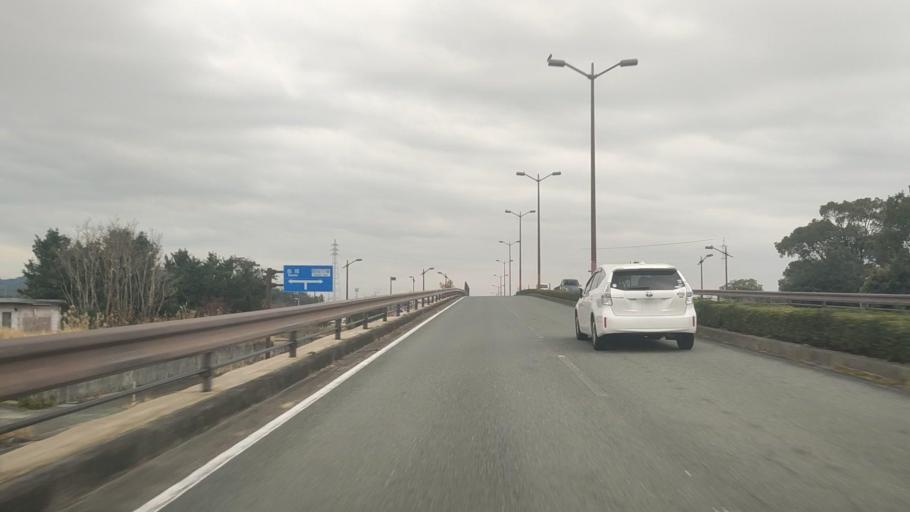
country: JP
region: Kumamoto
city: Ozu
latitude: 32.8369
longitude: 130.8031
